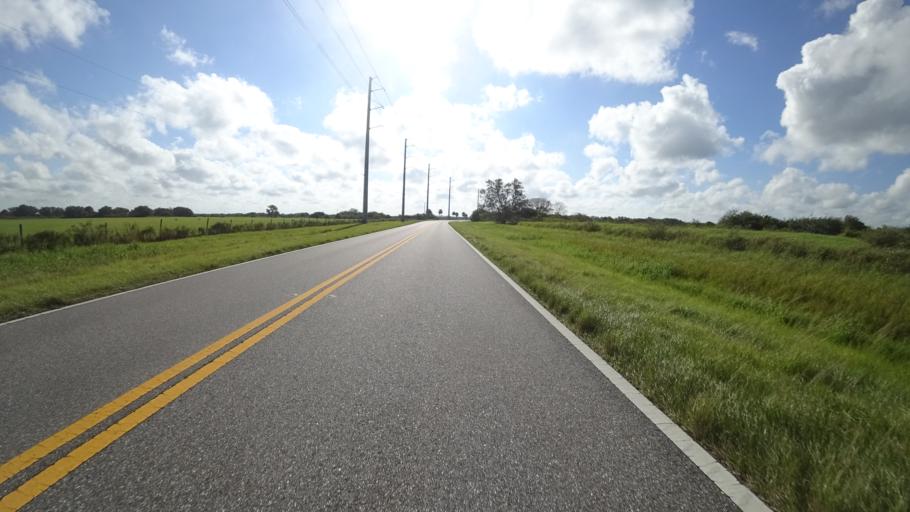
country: US
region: Florida
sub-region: Hillsborough County
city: Wimauma
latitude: 27.5143
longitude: -82.3235
